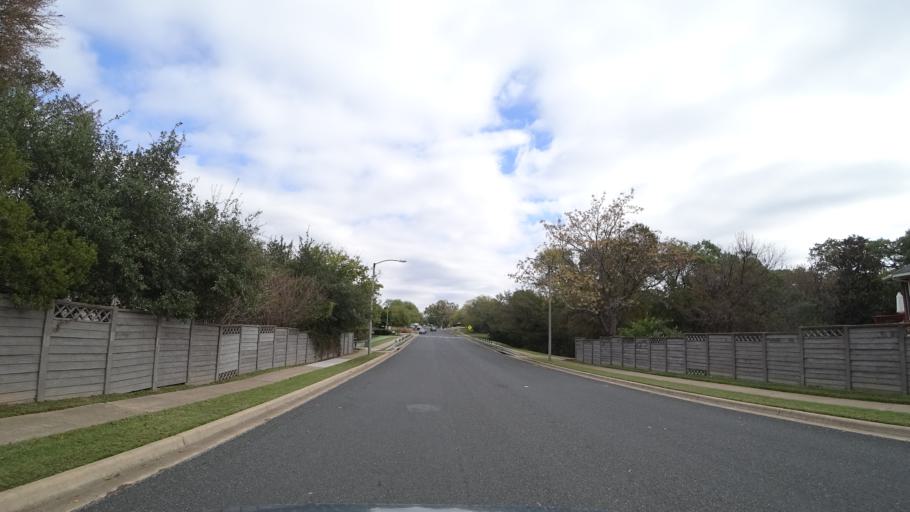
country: US
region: Texas
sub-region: Williamson County
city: Brushy Creek
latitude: 30.5132
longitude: -97.7426
